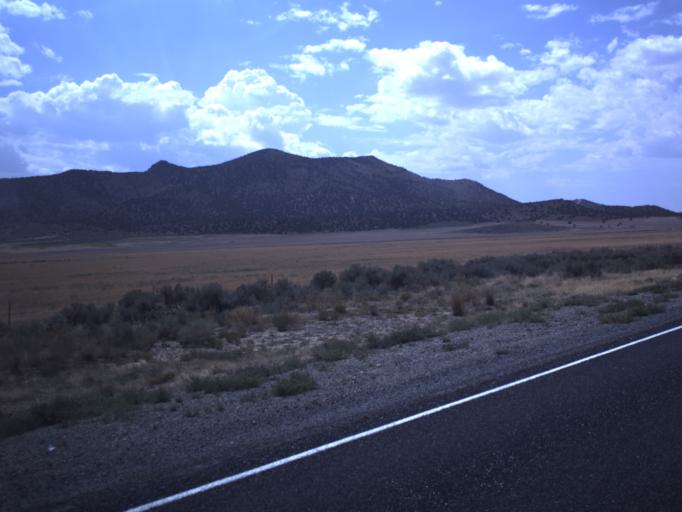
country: US
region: Utah
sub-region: Utah County
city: Eagle Mountain
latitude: 40.2450
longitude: -112.1372
